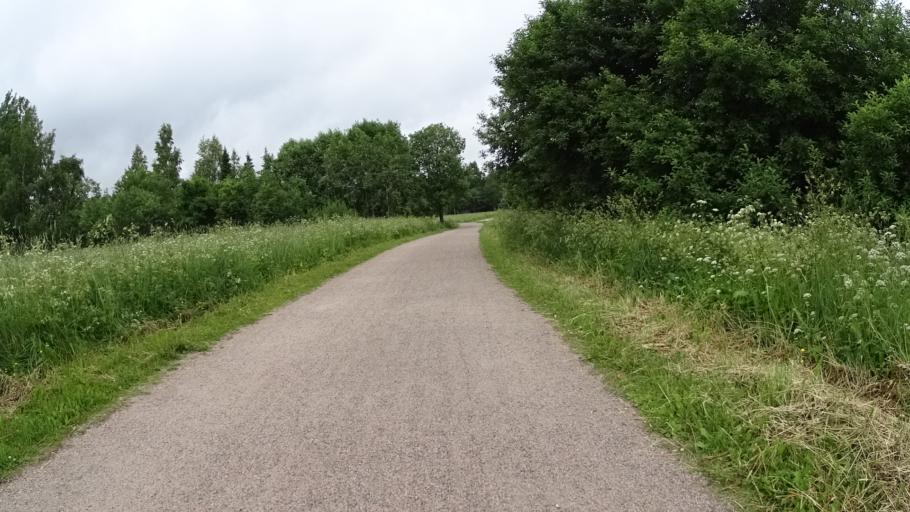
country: FI
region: Uusimaa
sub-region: Helsinki
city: Teekkarikylae
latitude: 60.2744
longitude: 24.8817
